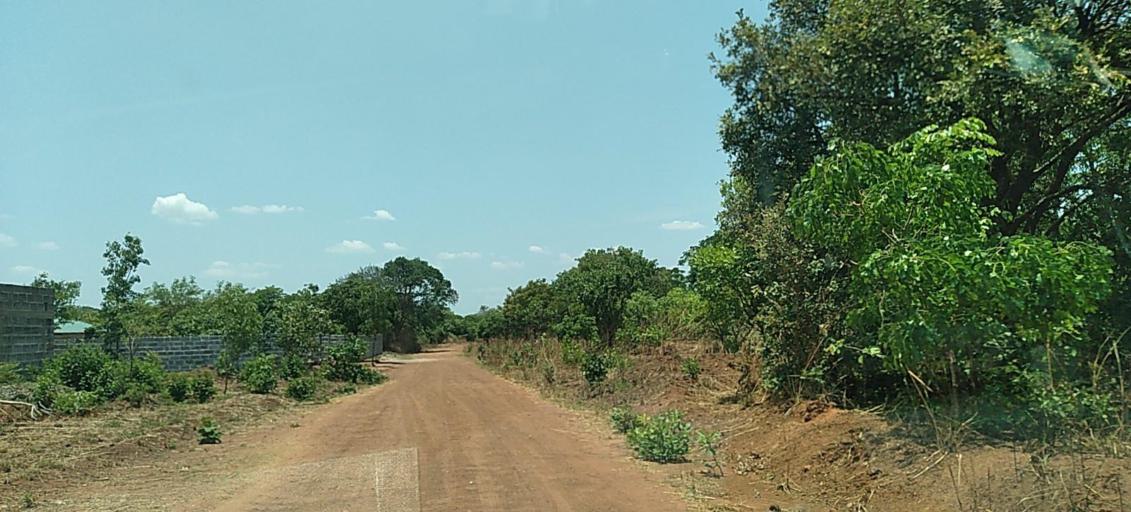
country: ZM
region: Copperbelt
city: Luanshya
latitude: -13.1022
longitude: 28.4047
